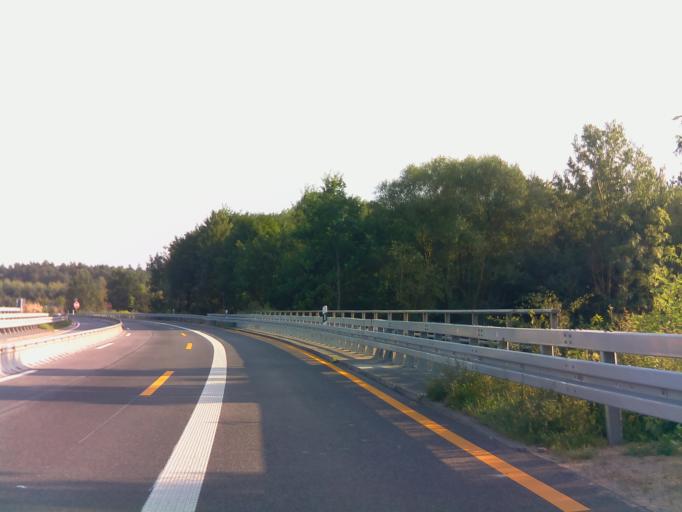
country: DE
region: Hesse
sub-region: Regierungsbezirk Darmstadt
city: Eppertshausen
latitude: 49.9511
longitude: 8.8306
